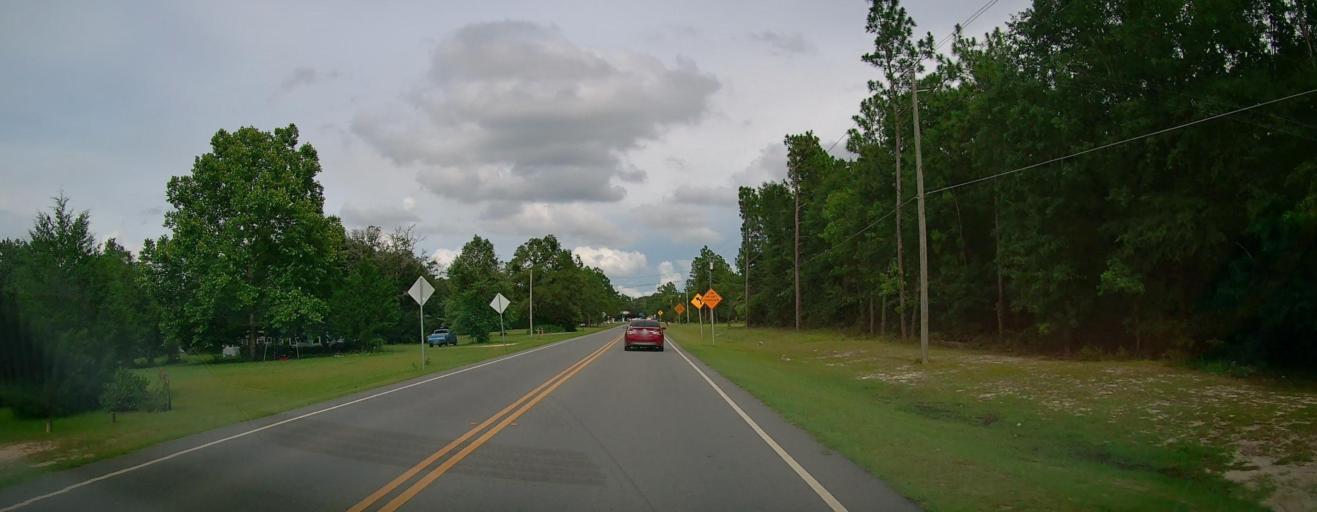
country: US
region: Georgia
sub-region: Wayne County
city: Jesup
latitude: 31.6574
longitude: -81.8965
